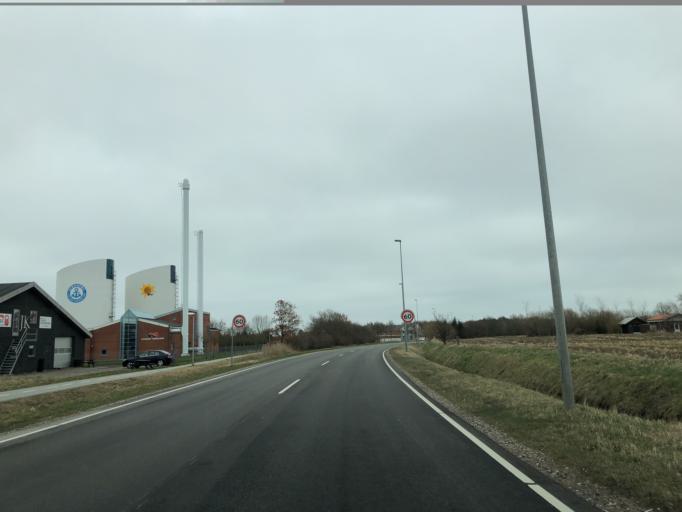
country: DK
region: North Denmark
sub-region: Frederikshavn Kommune
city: Strandby
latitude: 57.4864
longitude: 10.4868
